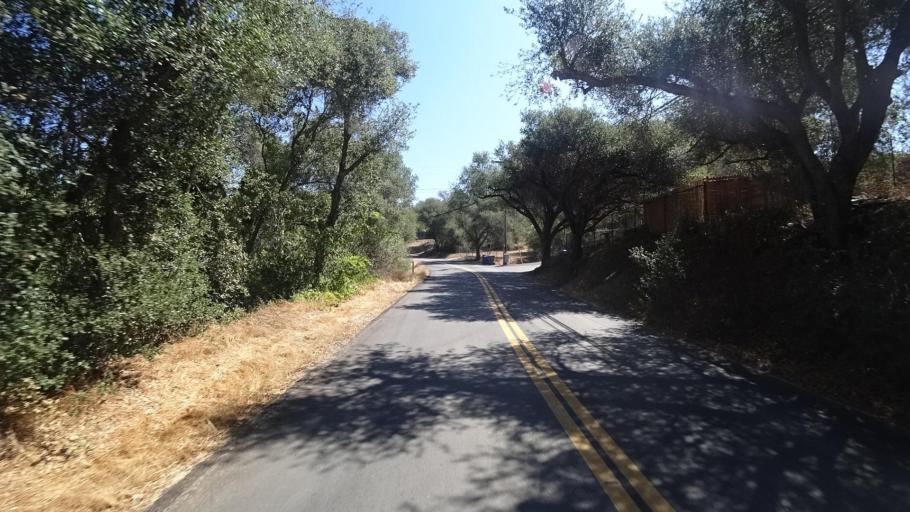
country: US
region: California
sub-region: San Diego County
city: Bonsall
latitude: 33.3341
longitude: -117.2313
